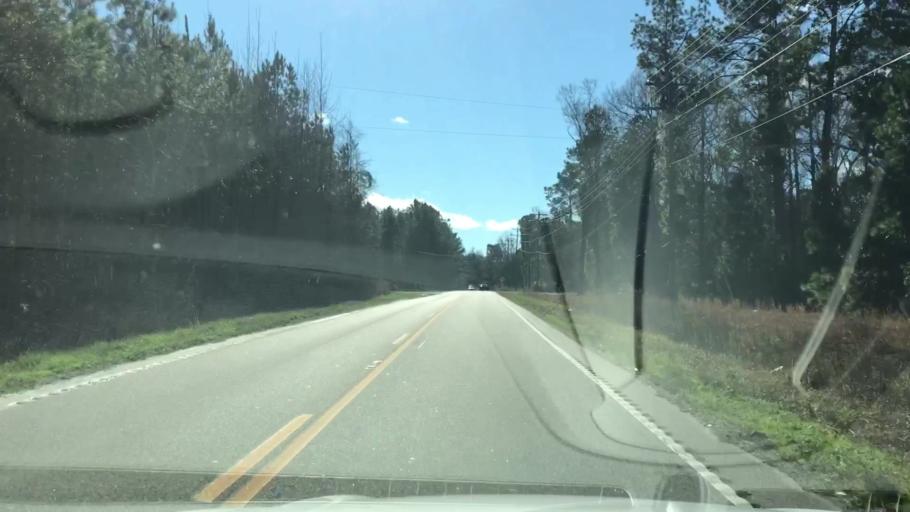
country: US
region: South Carolina
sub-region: Dorchester County
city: Summerville
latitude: 33.0711
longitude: -80.2207
